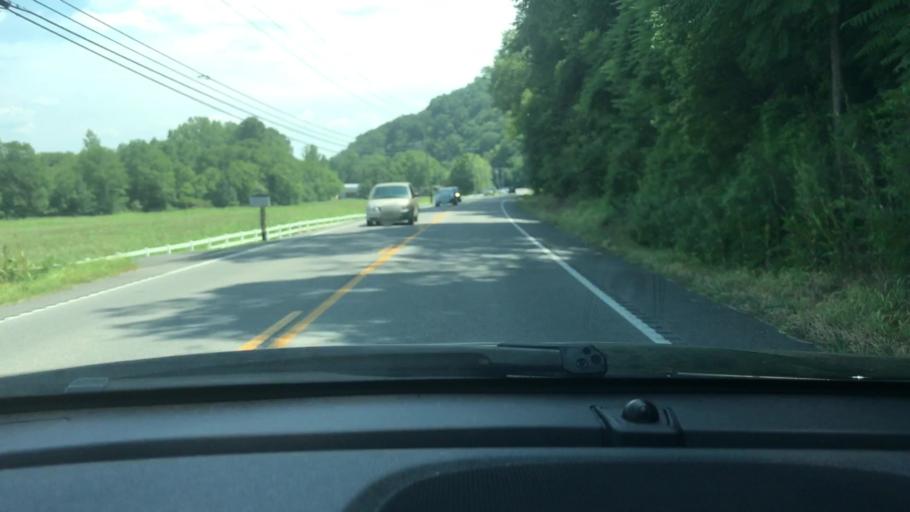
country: US
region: Tennessee
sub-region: Sumner County
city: Shackle Island
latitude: 36.3984
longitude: -86.6296
